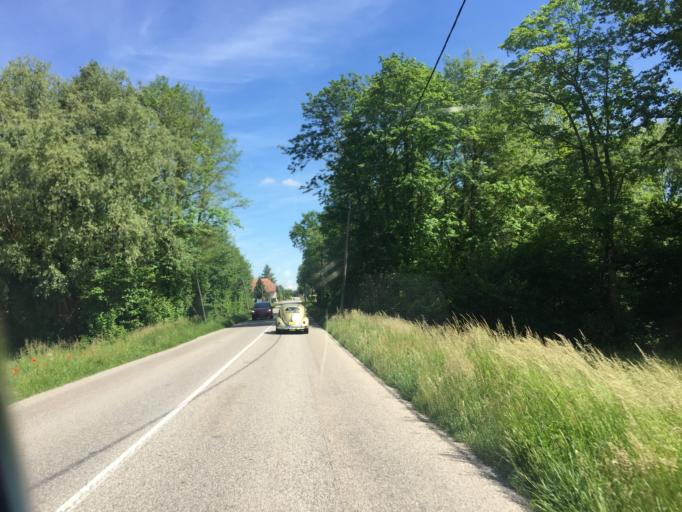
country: FR
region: Rhone-Alpes
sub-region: Departement de la Savoie
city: Albens
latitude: 45.8010
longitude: 5.9493
